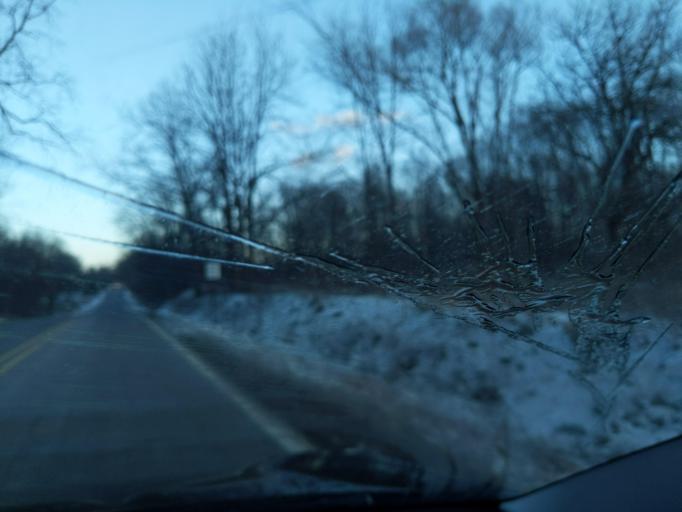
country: US
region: Michigan
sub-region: Ingham County
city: Stockbridge
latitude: 42.4540
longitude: -84.2092
